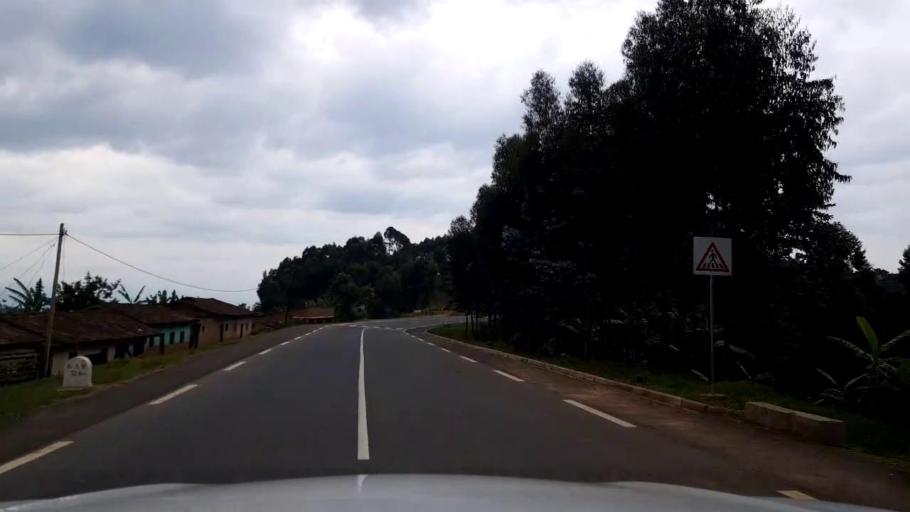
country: RW
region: Western Province
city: Kibuye
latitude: -1.8885
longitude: 29.3457
